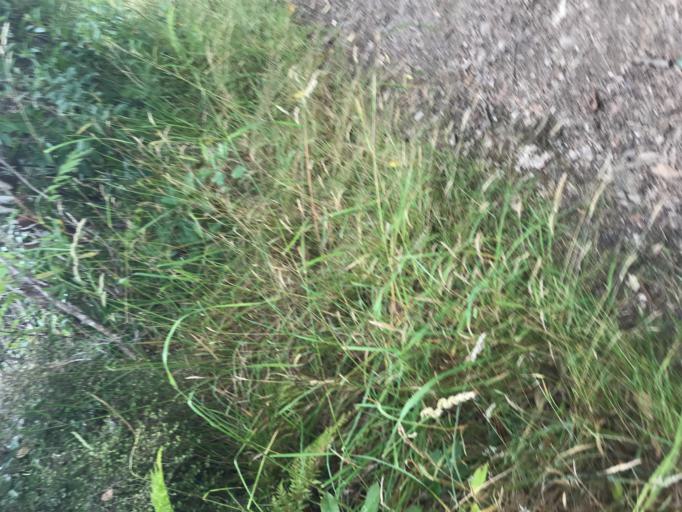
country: NZ
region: Marlborough
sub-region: Marlborough District
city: Picton
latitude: -41.2186
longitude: 173.9740
